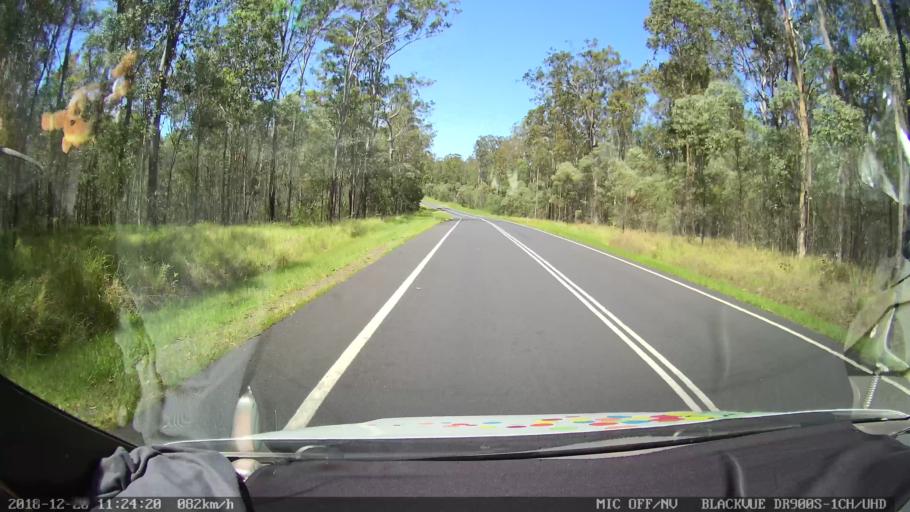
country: AU
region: New South Wales
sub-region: Richmond Valley
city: Casino
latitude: -29.0729
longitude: 153.0026
